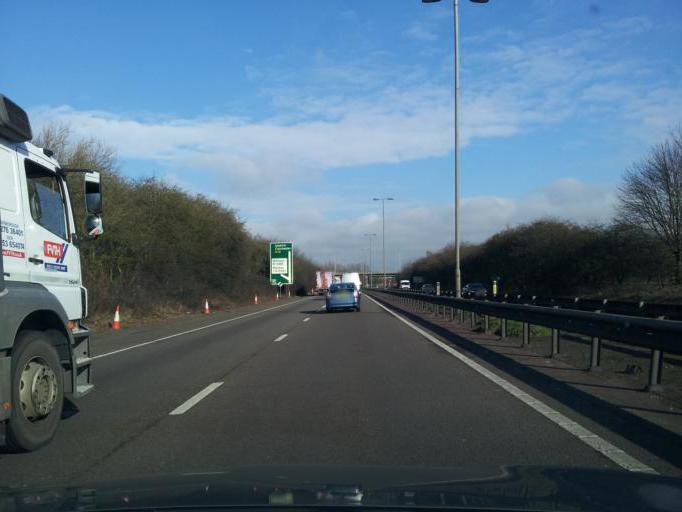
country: GB
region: England
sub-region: Essex
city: Witham
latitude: 51.8053
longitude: 0.6528
